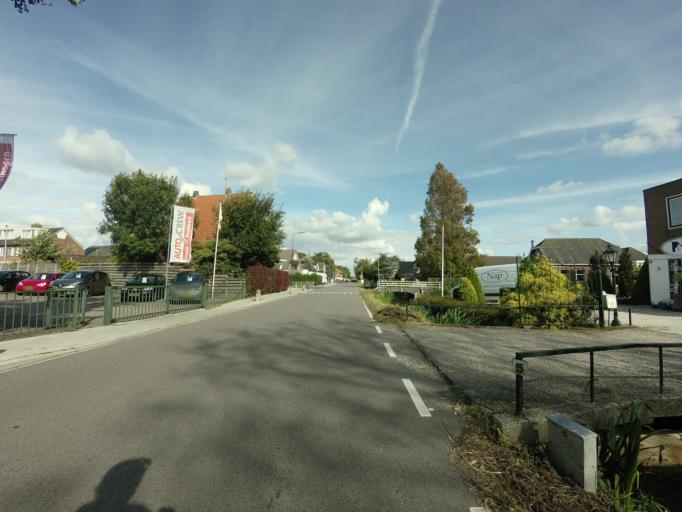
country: NL
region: Utrecht
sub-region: Gemeente De Ronde Venen
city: Mijdrecht
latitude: 52.1949
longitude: 4.9004
